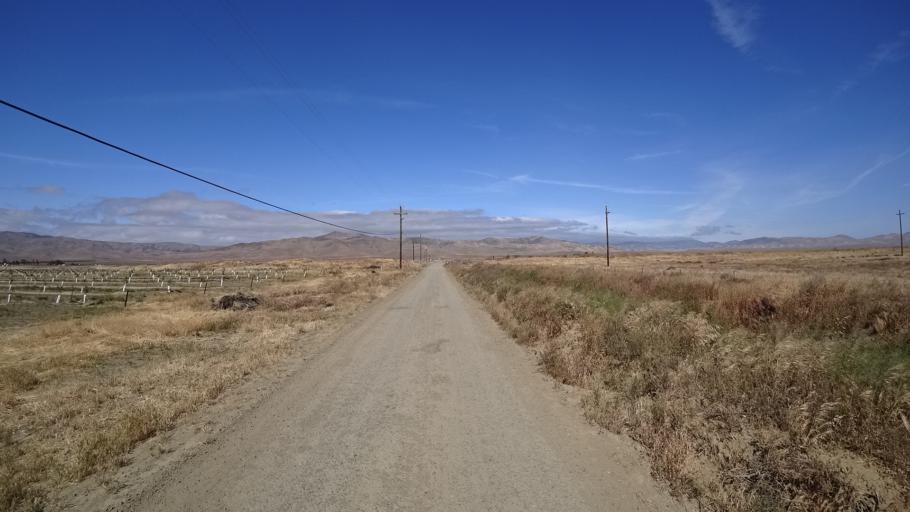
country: US
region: California
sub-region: Kings County
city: Avenal
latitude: 35.8180
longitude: -120.0810
